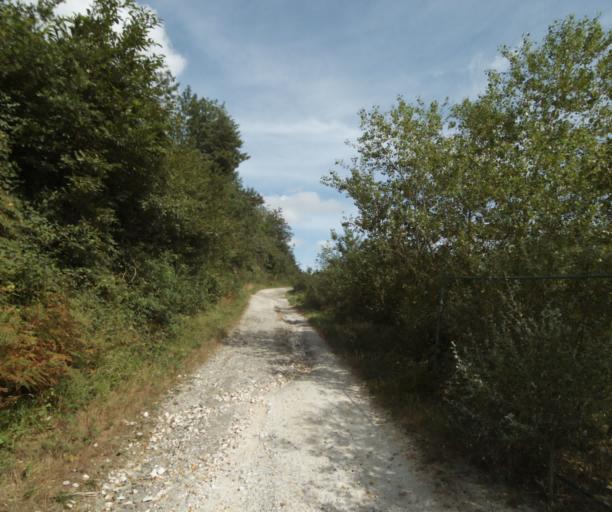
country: FR
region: Midi-Pyrenees
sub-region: Departement du Tarn
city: Soreze
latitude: 43.4557
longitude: 2.1076
